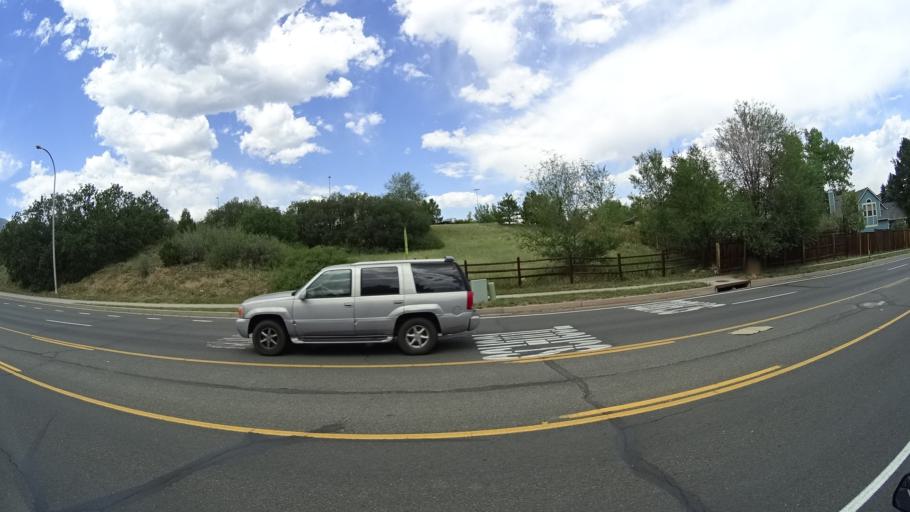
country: US
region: Colorado
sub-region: El Paso County
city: Stratmoor
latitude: 38.7833
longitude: -104.7990
